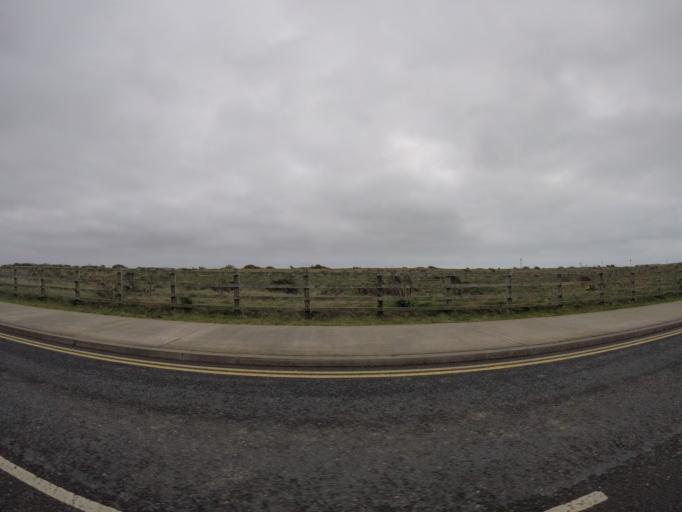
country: IE
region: Munster
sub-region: Waterford
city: Tra Mhor
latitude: 52.1626
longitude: -7.1351
